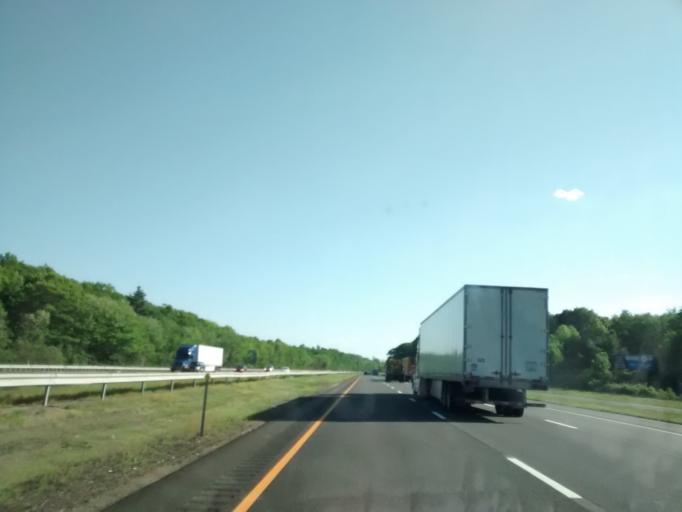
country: US
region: Connecticut
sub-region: Tolland County
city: Stafford
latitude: 41.9569
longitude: -72.1974
